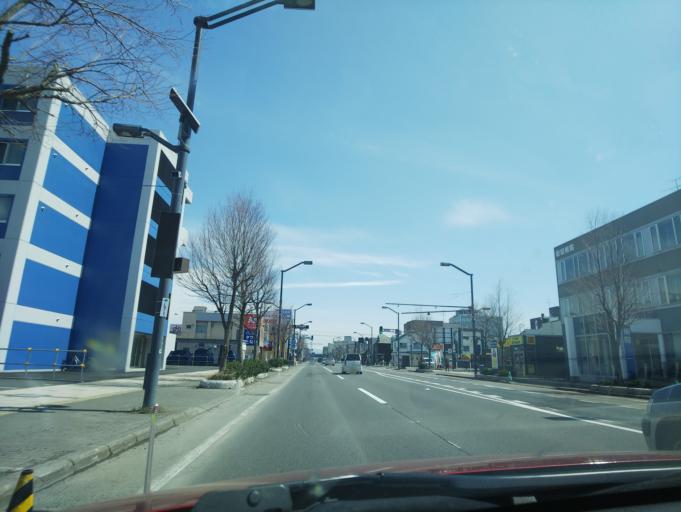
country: JP
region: Hokkaido
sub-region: Asahikawa-shi
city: Asahikawa
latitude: 43.7666
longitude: 142.3691
